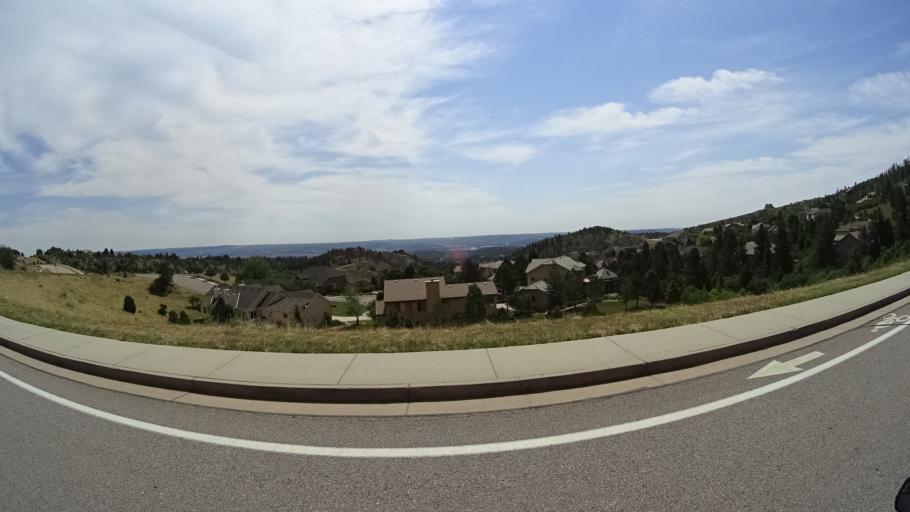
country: US
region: Colorado
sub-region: El Paso County
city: Air Force Academy
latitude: 38.9494
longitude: -104.8860
